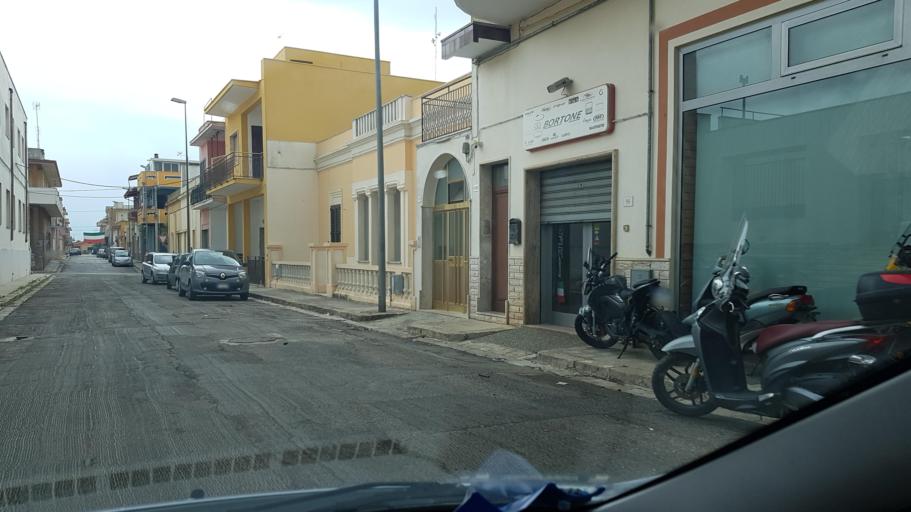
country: IT
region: Apulia
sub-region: Provincia di Lecce
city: Taurisano
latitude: 39.9532
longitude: 18.2177
